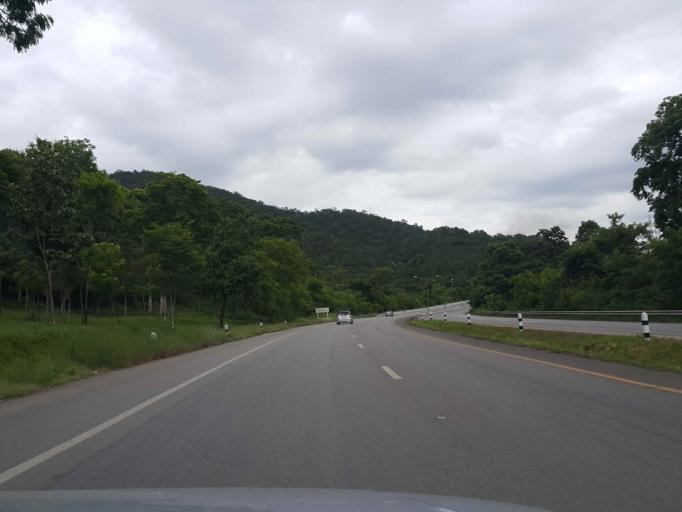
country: TH
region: Lampang
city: Lampang
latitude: 18.2529
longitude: 99.5627
